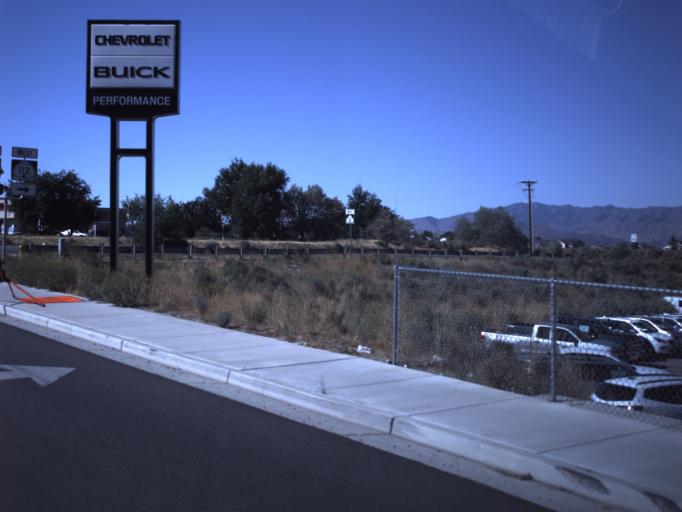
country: US
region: Utah
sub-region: Tooele County
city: Tooele
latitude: 40.5515
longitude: -112.2981
